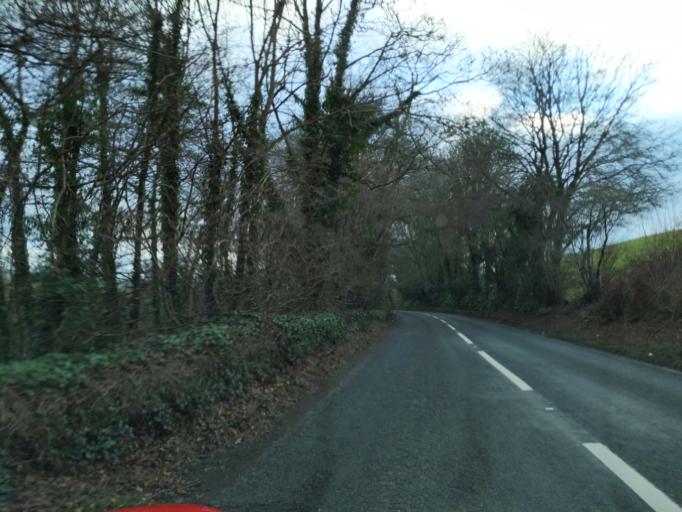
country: GB
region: England
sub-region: Cornwall
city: Pillaton
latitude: 50.3777
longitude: -4.3058
